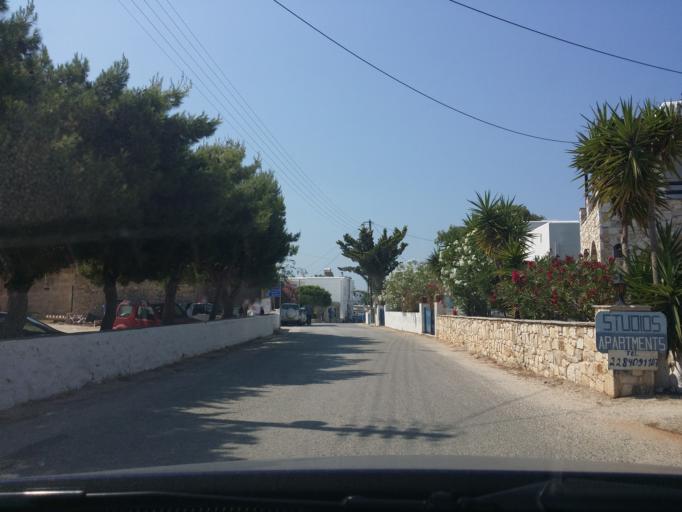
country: GR
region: South Aegean
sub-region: Nomos Kykladon
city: Antiparos
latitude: 36.9978
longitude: 25.1363
